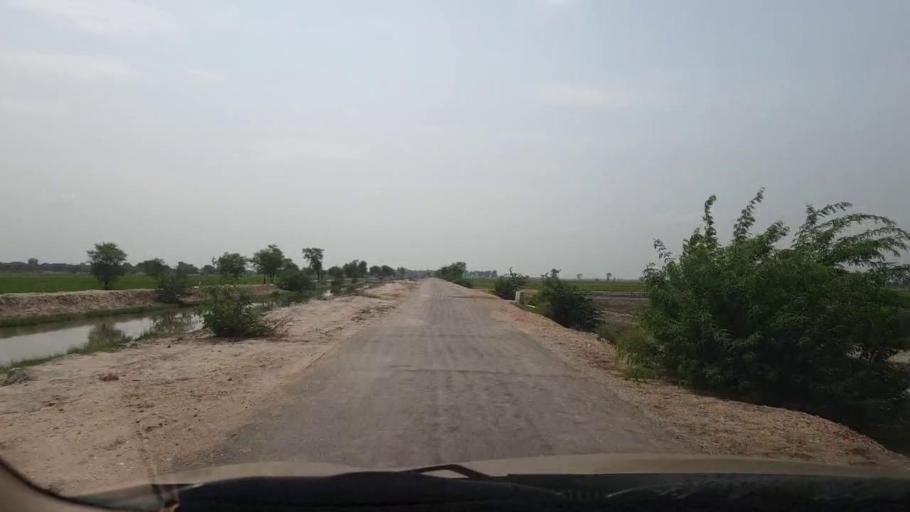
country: PK
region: Sindh
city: Goth Garelo
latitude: 27.5153
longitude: 68.1054
